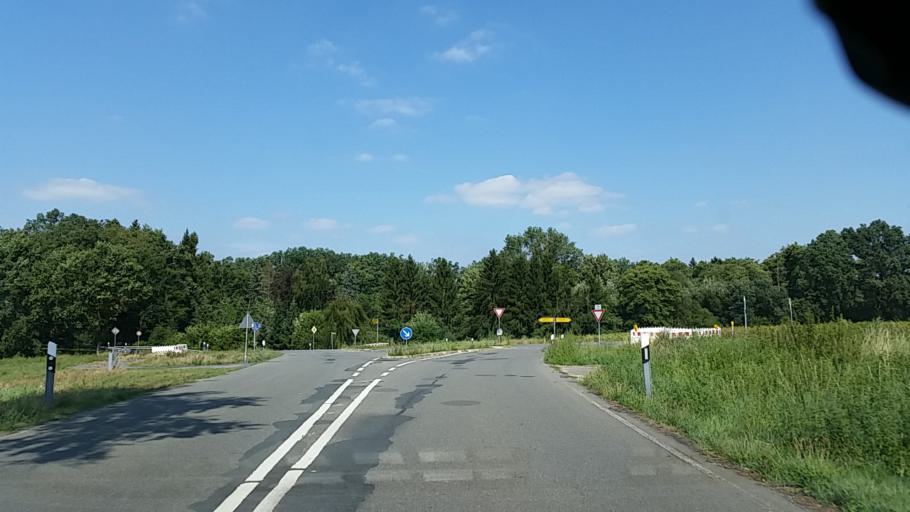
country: DE
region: Lower Saxony
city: Jelmstorf
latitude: 53.1306
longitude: 10.5301
